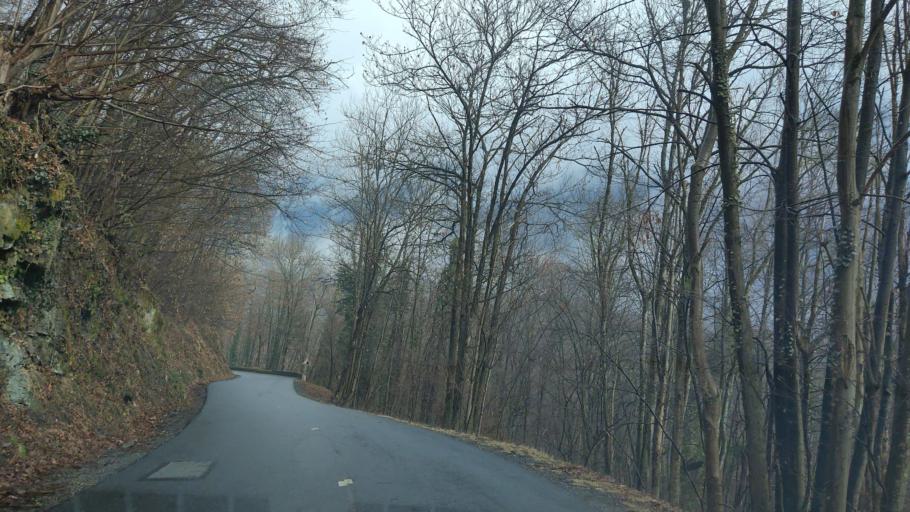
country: FR
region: Rhone-Alpes
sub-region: Departement de la Savoie
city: Aiton
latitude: 45.5328
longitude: 6.3072
